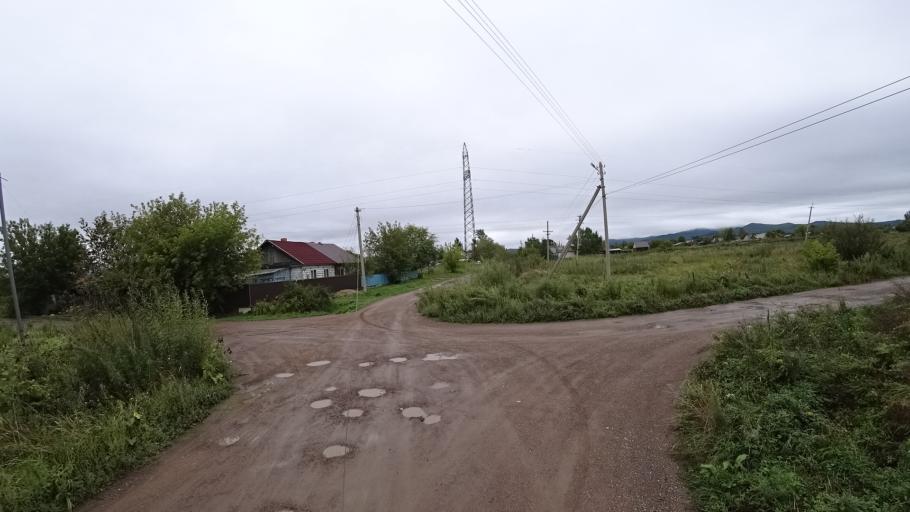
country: RU
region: Primorskiy
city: Monastyrishche
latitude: 44.2003
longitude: 132.4736
